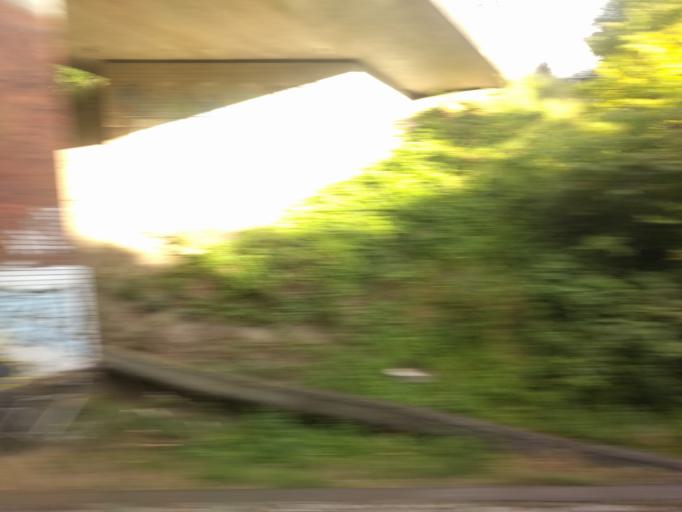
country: DK
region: Zealand
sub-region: Slagelse Kommune
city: Slagelse
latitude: 55.4115
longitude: 11.3619
